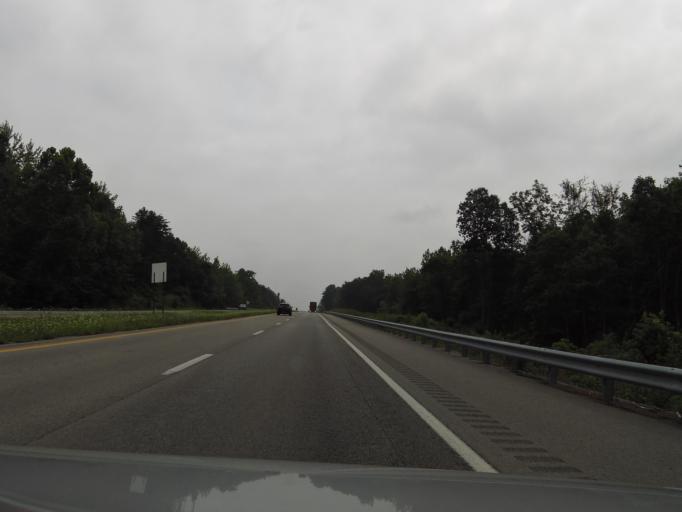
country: US
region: Kentucky
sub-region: Muhlenberg County
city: Central City
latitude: 37.2997
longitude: -87.0718
